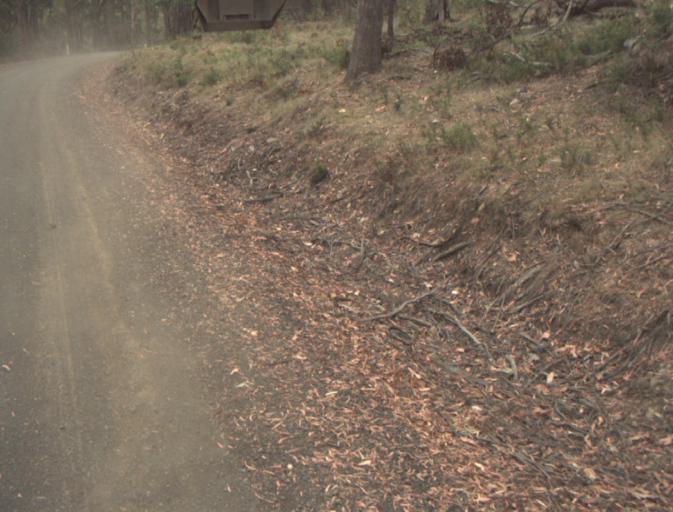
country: AU
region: Tasmania
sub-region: Northern Midlands
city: Evandale
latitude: -41.4895
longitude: 147.5461
